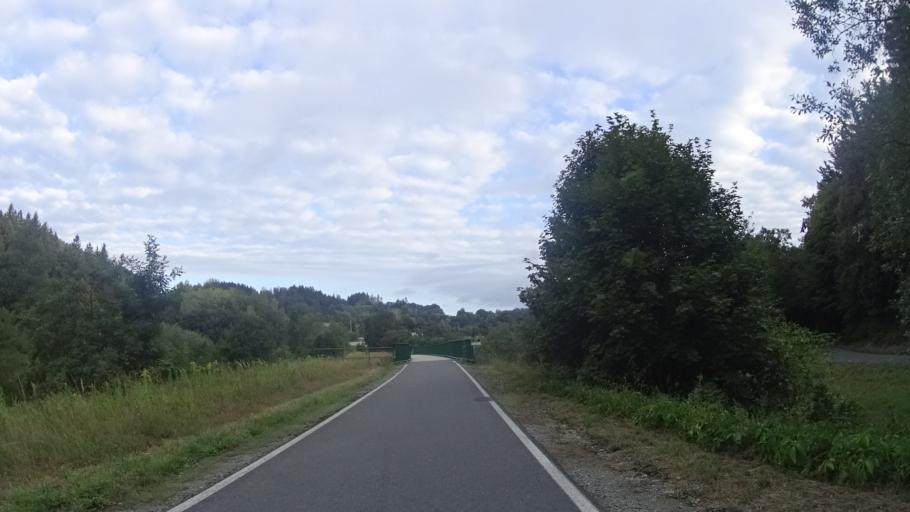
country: CZ
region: Olomoucky
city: Zabreh
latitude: 49.8617
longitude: 16.8201
